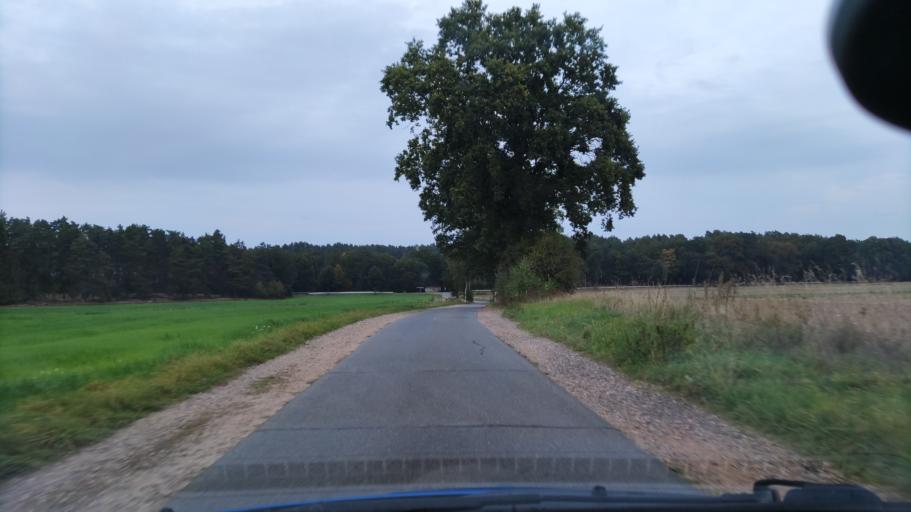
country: DE
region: Lower Saxony
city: Karwitz
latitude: 53.1058
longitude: 11.0192
